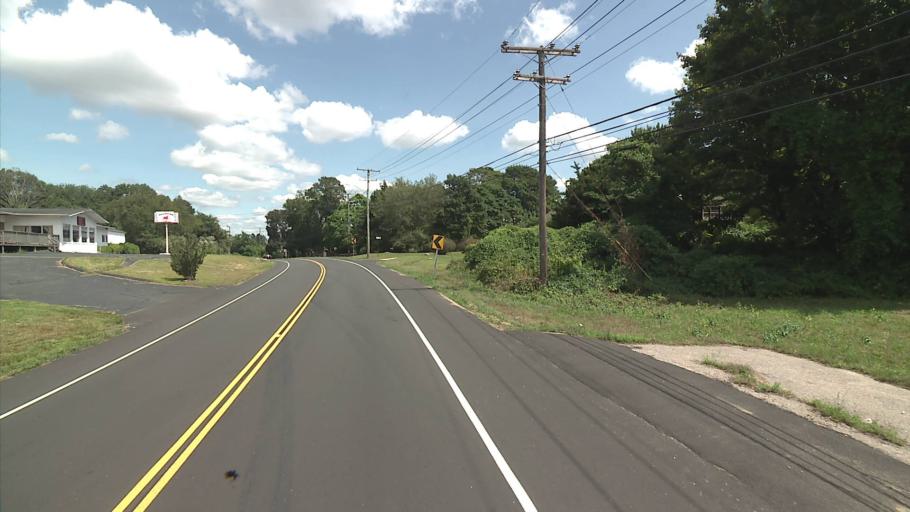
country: US
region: Connecticut
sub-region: New London County
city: Pawcatuck
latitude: 41.3527
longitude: -71.8858
